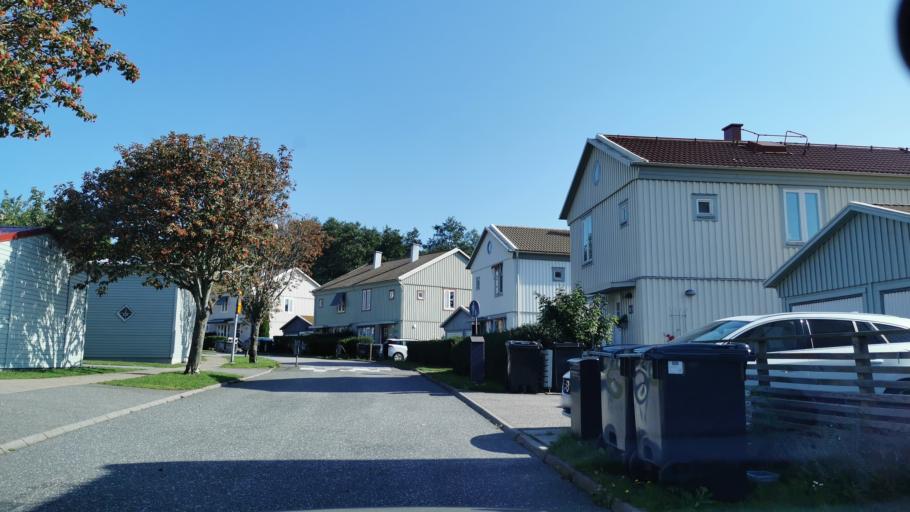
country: SE
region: Vaestra Goetaland
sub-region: Molndal
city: Moelndal
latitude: 57.6551
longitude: 11.9625
